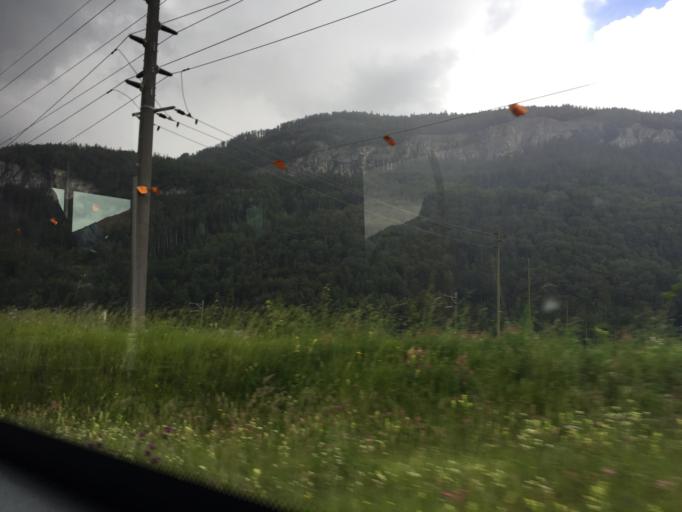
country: CH
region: Bern
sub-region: Interlaken-Oberhasli District
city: Meiringen
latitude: 46.7405
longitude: 8.1479
